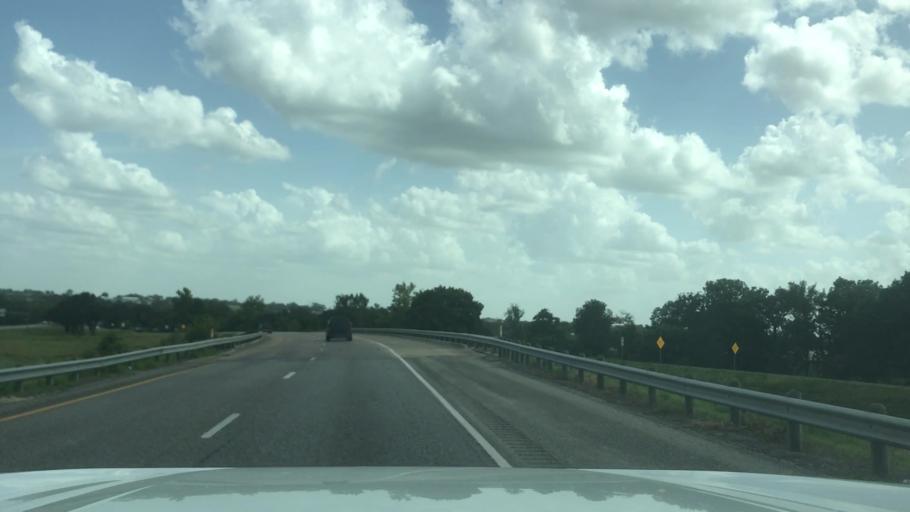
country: US
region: Texas
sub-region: Grimes County
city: Navasota
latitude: 30.3443
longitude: -96.0516
